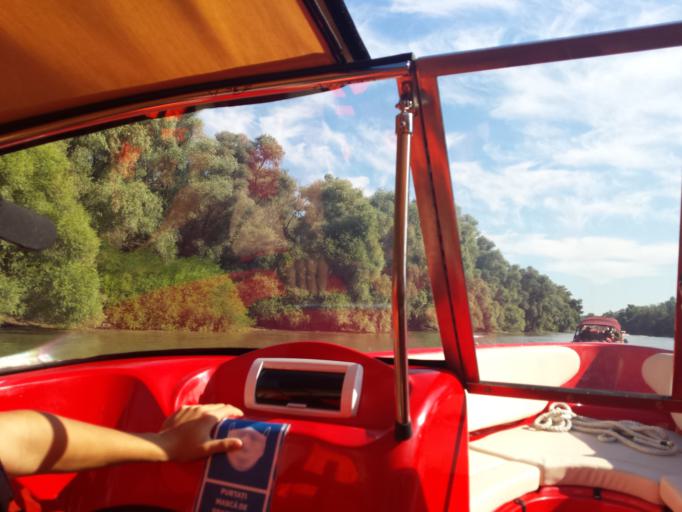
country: RO
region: Tulcea
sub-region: Comuna Nufaru
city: Nufaru
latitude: 45.2209
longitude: 28.8801
